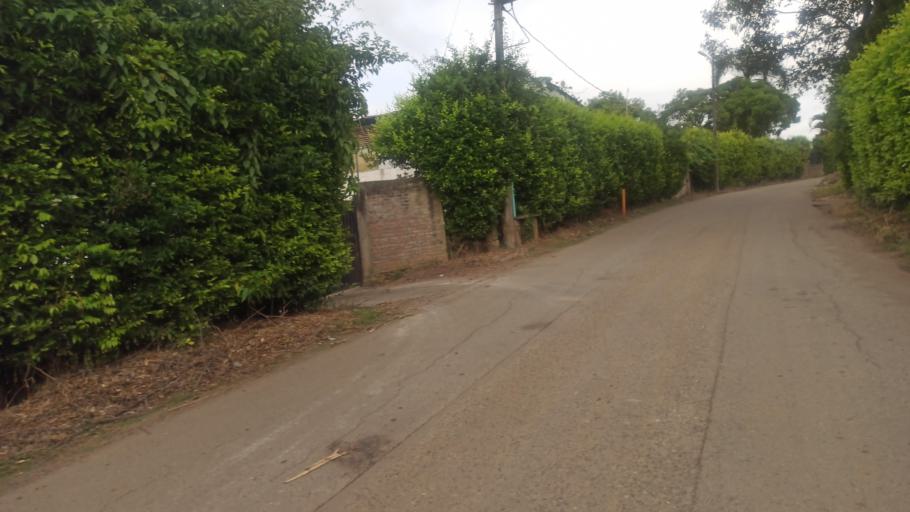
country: CO
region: Valle del Cauca
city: Jamundi
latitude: 3.2022
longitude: -76.5108
